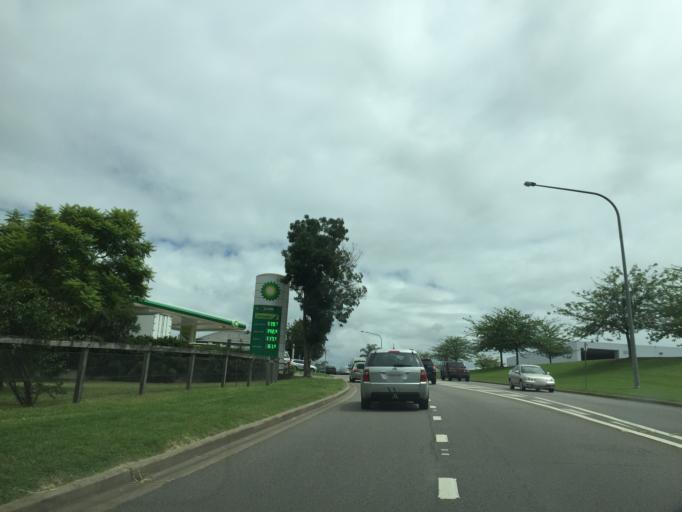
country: AU
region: New South Wales
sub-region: Hawkesbury
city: Richmond
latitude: -33.5834
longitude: 150.7230
